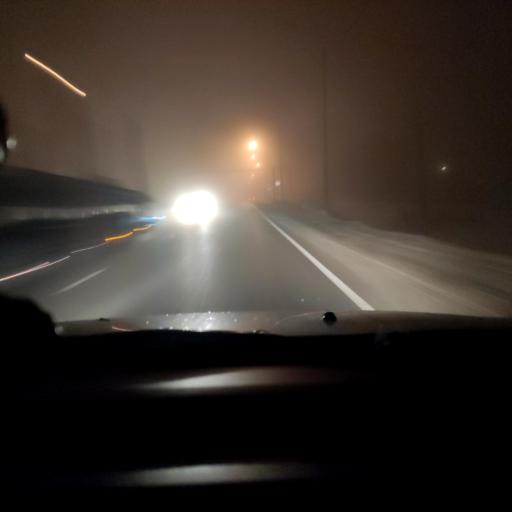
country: RU
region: Samara
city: Dubovyy Umet
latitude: 52.9624
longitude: 50.2899
